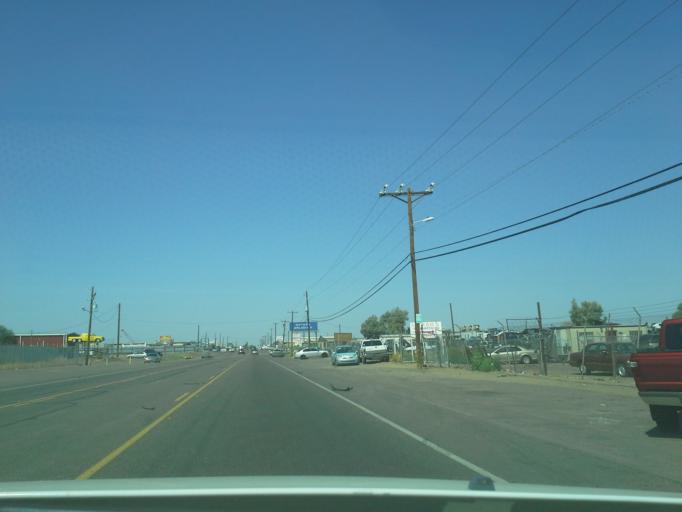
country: US
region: Arizona
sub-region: Maricopa County
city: Laveen
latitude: 33.4067
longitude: -112.1239
